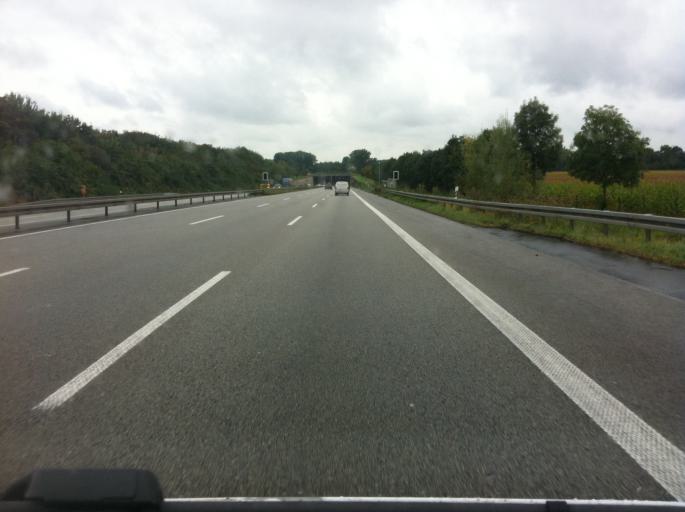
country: DE
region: North Rhine-Westphalia
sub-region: Regierungsbezirk Dusseldorf
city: Meerbusch
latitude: 51.2818
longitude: 6.6946
